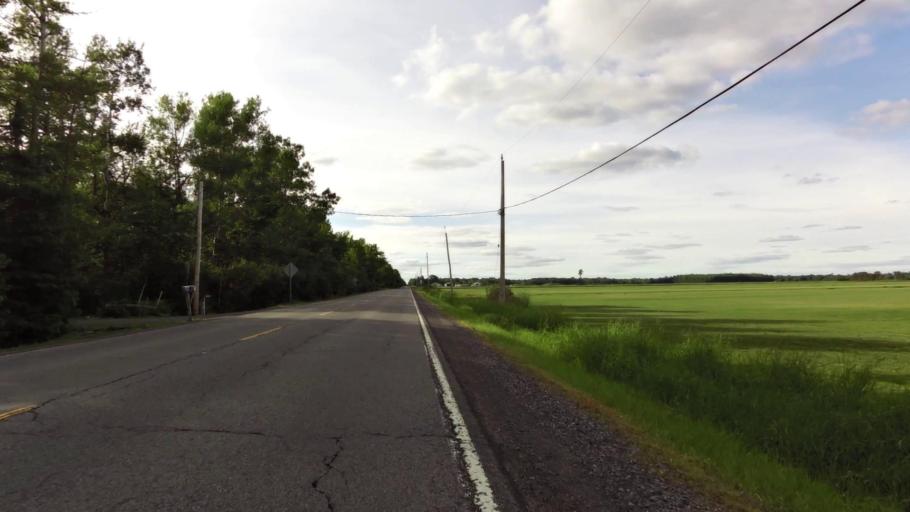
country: CA
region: Ontario
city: Ottawa
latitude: 45.1900
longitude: -75.5856
